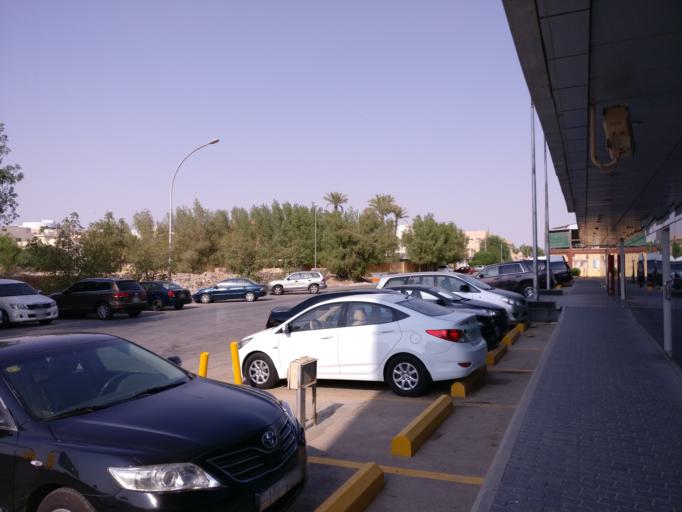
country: SA
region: Ar Riyad
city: Riyadh
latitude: 24.6935
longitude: 46.7324
